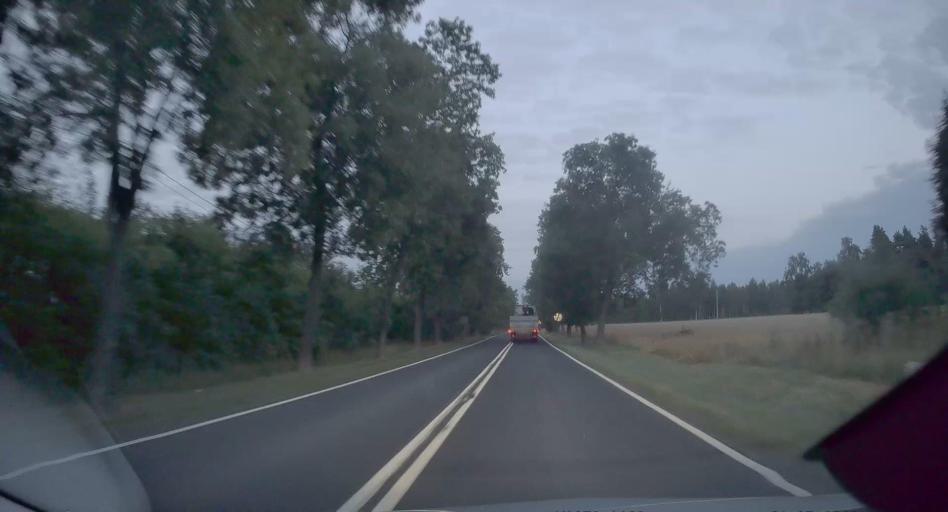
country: PL
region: Silesian Voivodeship
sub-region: Powiat klobucki
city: Opatow
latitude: 50.9555
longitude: 18.7940
